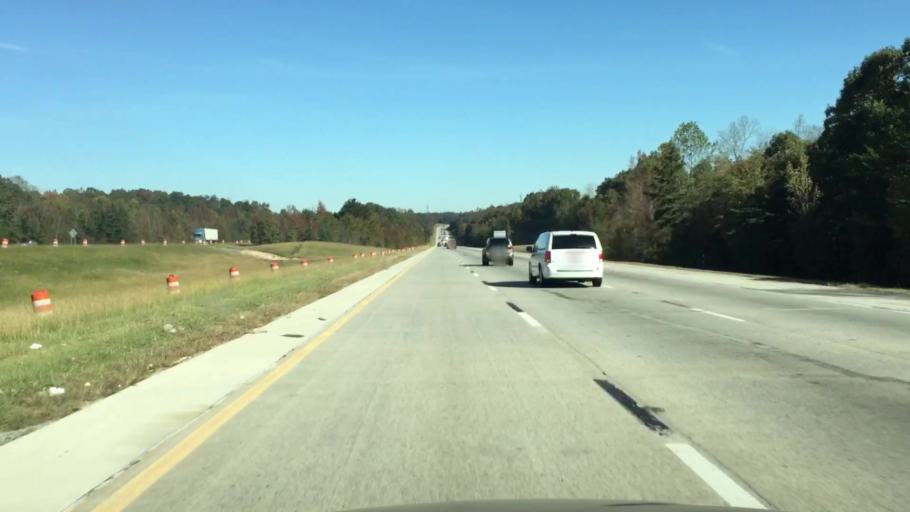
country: US
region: North Carolina
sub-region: Guilford County
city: Jamestown
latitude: 35.9648
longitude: -79.8931
